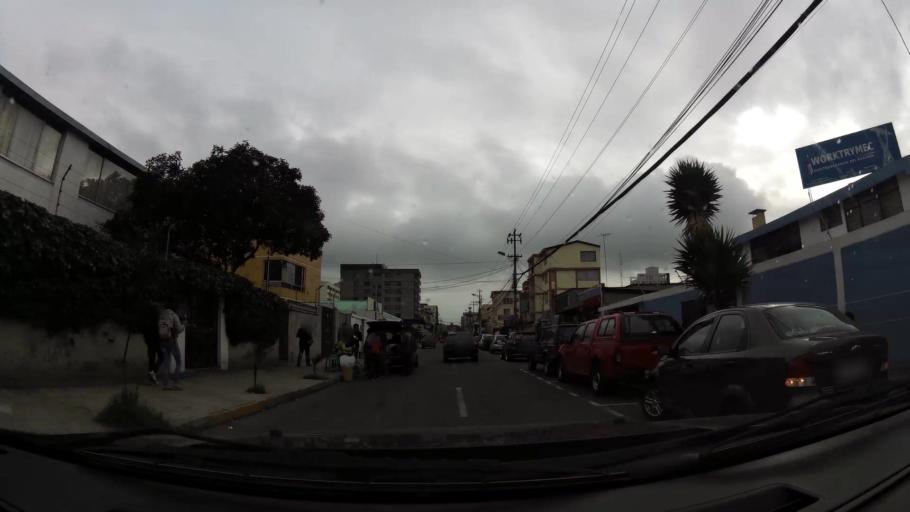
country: EC
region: Pichincha
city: Quito
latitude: -0.1921
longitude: -78.4923
